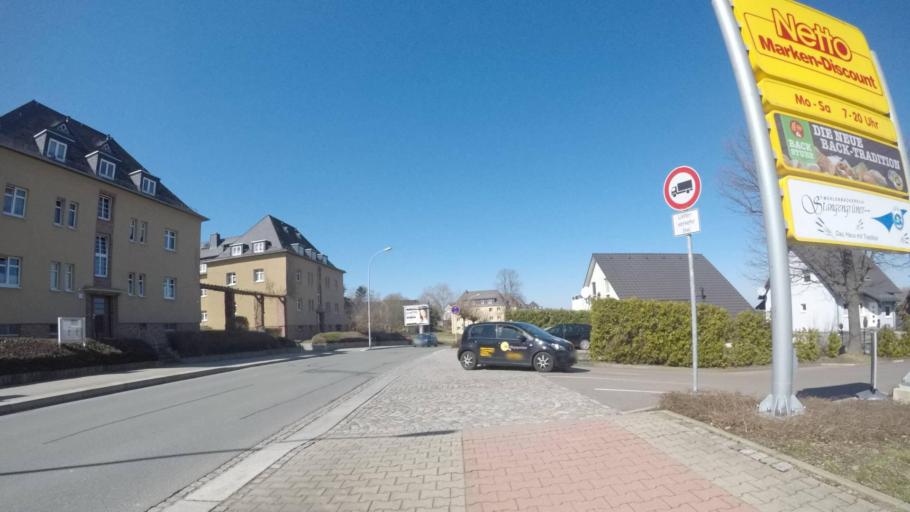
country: DE
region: Saxony
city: Limbach-Oberfrohna
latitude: 50.8630
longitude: 12.7575
